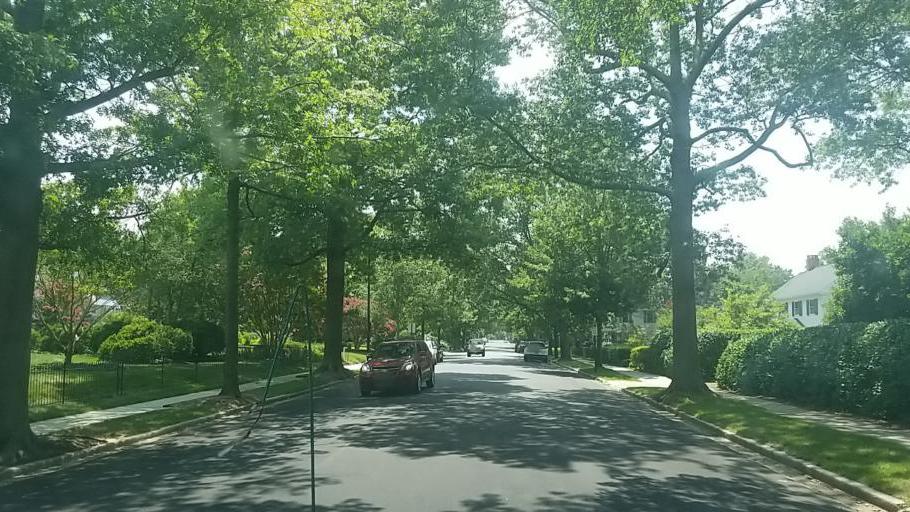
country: US
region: Maryland
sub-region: Talbot County
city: Easton
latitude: 38.7690
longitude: -76.0742
